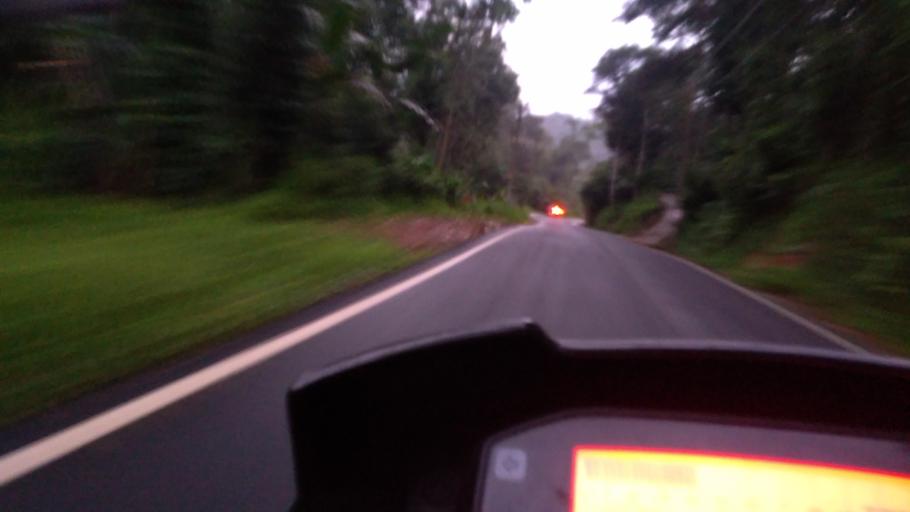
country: IN
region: Kerala
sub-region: Idukki
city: Munnar
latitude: 9.9574
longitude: 77.0800
